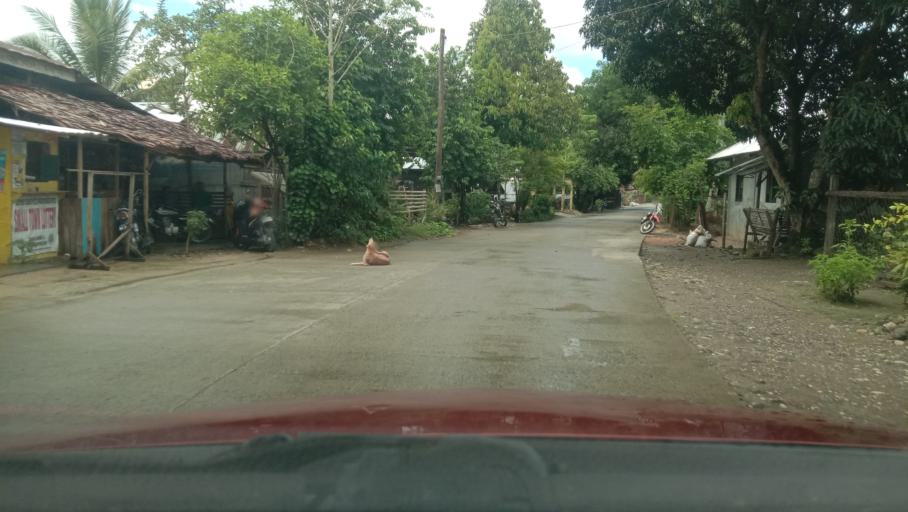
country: PH
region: Caraga
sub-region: Province of Agusan del Sur
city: Patin-ay
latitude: 8.5537
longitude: 125.9481
